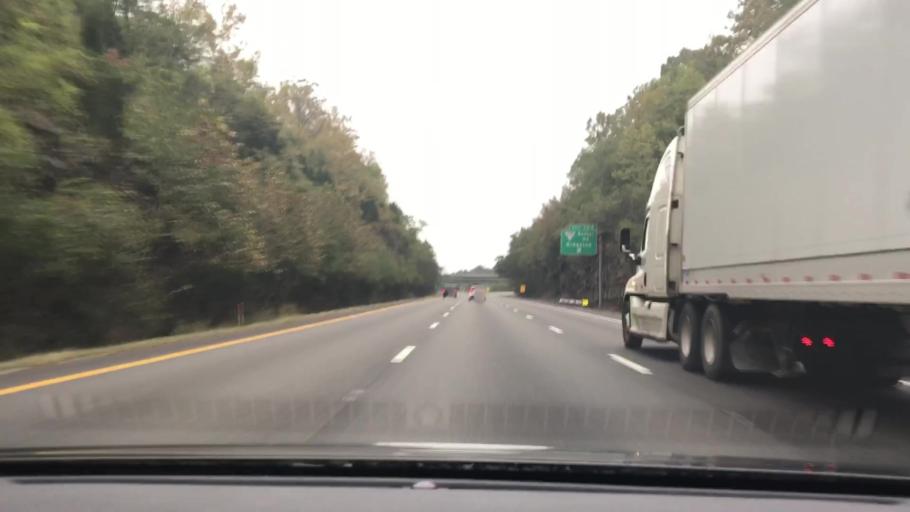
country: US
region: Tennessee
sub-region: Sumner County
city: Millersville
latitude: 36.4146
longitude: -86.7194
